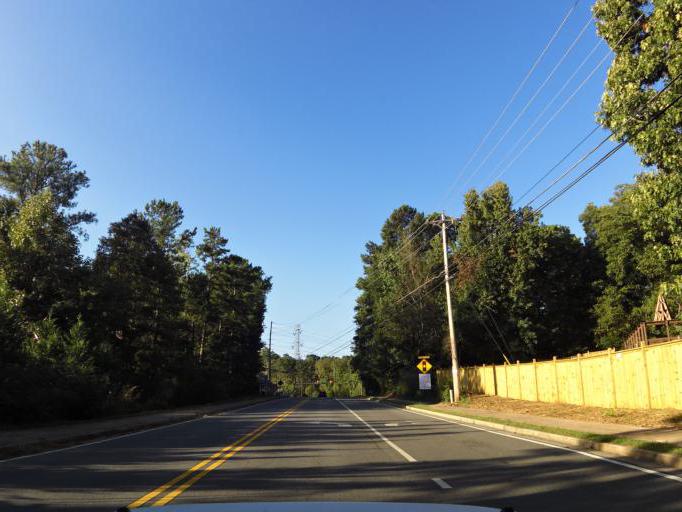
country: US
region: Georgia
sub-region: Cobb County
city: Kennesaw
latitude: 33.9989
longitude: -84.6428
